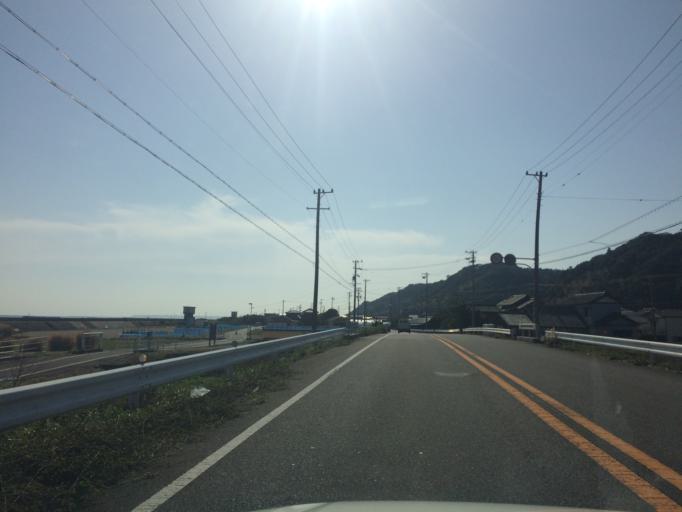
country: JP
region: Shizuoka
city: Sagara
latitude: 34.7118
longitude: 138.2141
